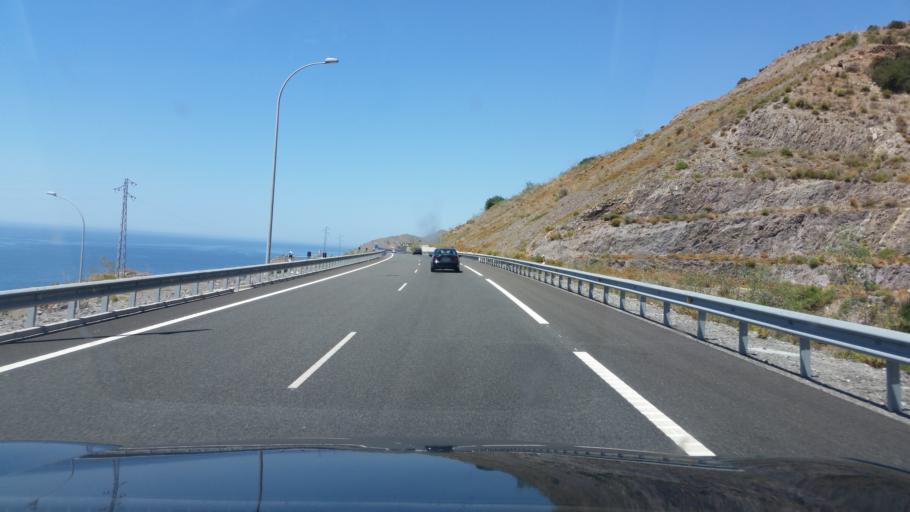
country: ES
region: Andalusia
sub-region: Provincia de Granada
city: Sorvilan
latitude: 36.7570
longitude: -3.2566
